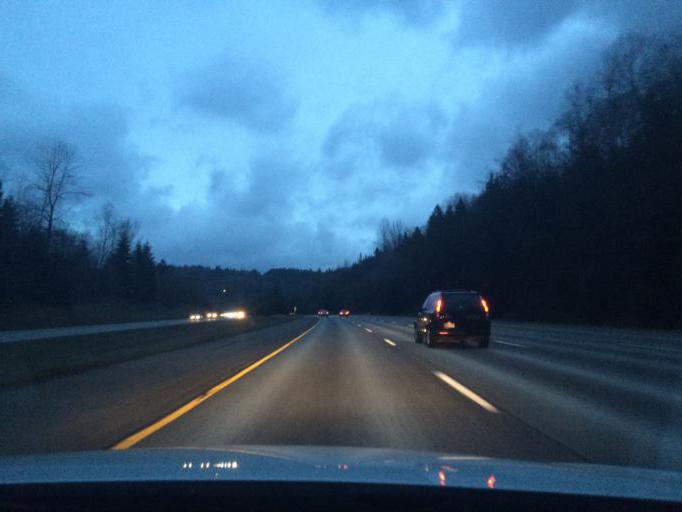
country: US
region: Washington
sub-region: King County
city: Issaquah
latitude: 47.5320
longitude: -121.9945
